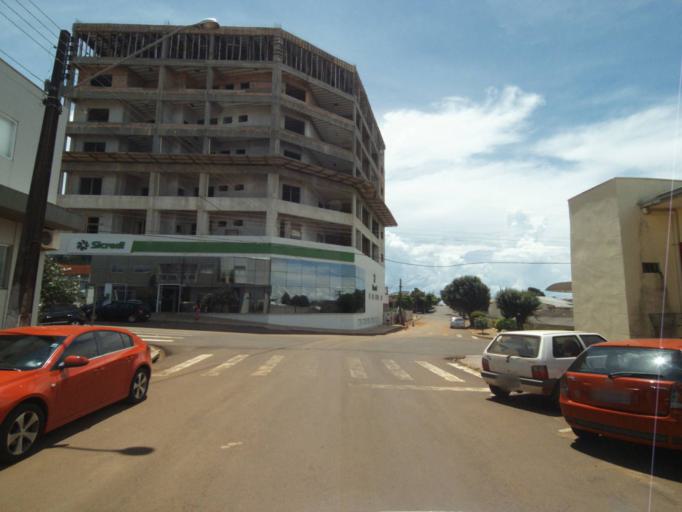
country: BR
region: Parana
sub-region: Guaraniacu
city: Guaraniacu
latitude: -25.0986
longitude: -52.8686
